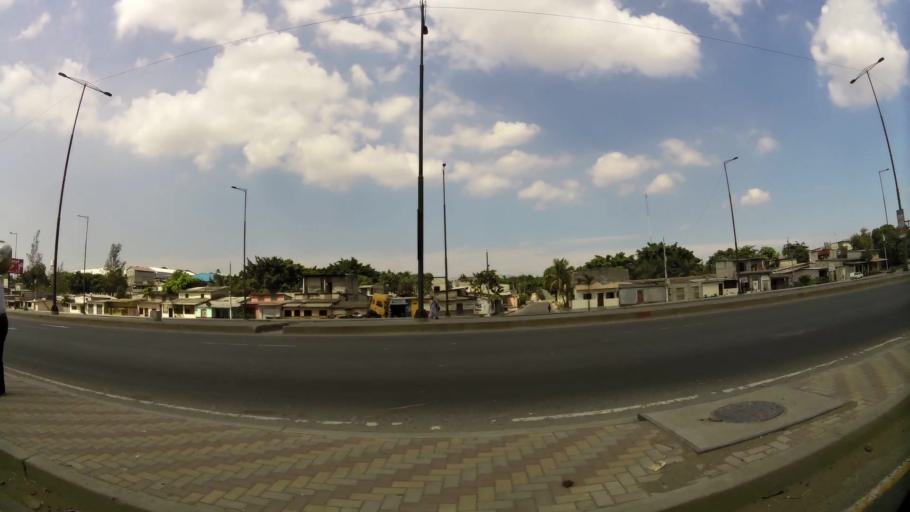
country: EC
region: Guayas
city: Santa Lucia
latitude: -2.1230
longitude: -79.9494
